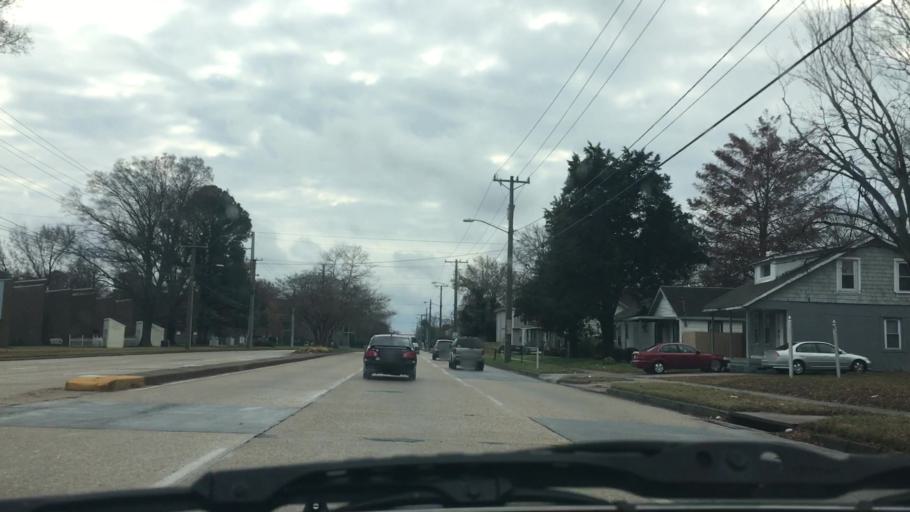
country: US
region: Virginia
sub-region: City of Norfolk
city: Norfolk
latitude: 36.9114
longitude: -76.2410
